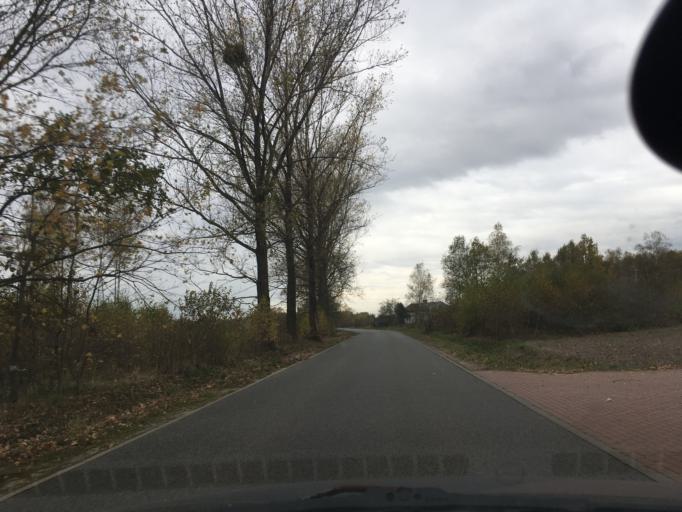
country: PL
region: Lodz Voivodeship
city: Zabia Wola
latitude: 52.0204
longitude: 20.7210
